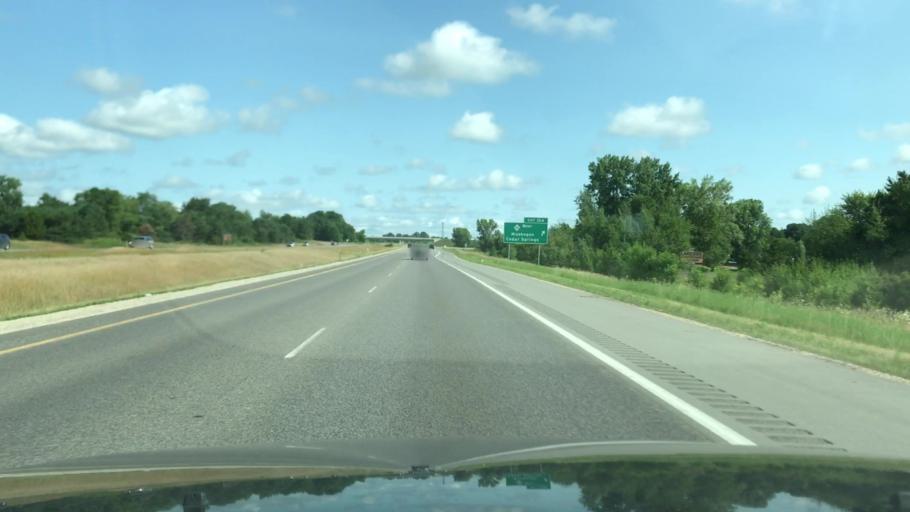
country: US
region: Michigan
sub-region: Kent County
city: Cedar Springs
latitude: 43.2110
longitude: -85.5749
